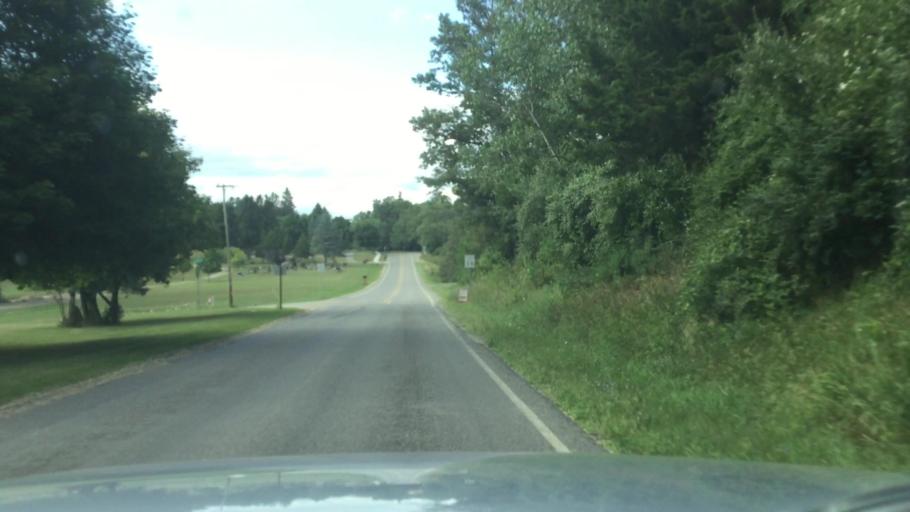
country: US
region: Michigan
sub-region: Ionia County
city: Belding
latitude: 43.0776
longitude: -85.2281
